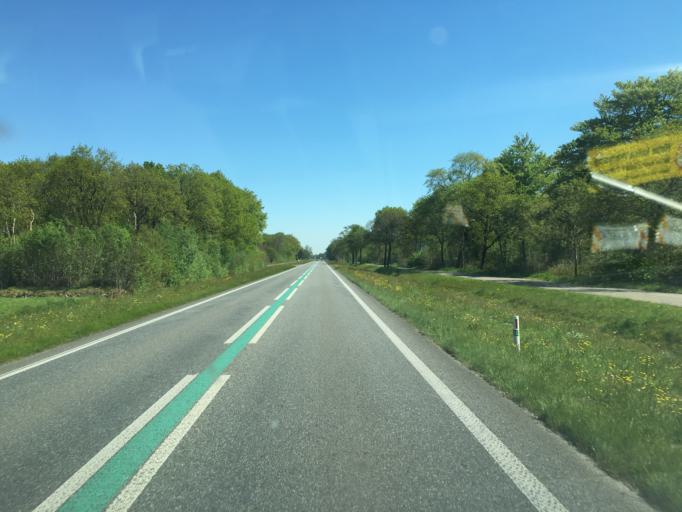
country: NL
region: Friesland
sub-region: Gemeente Gaasterlan-Sleat
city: Balk
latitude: 52.8814
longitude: 5.5532
